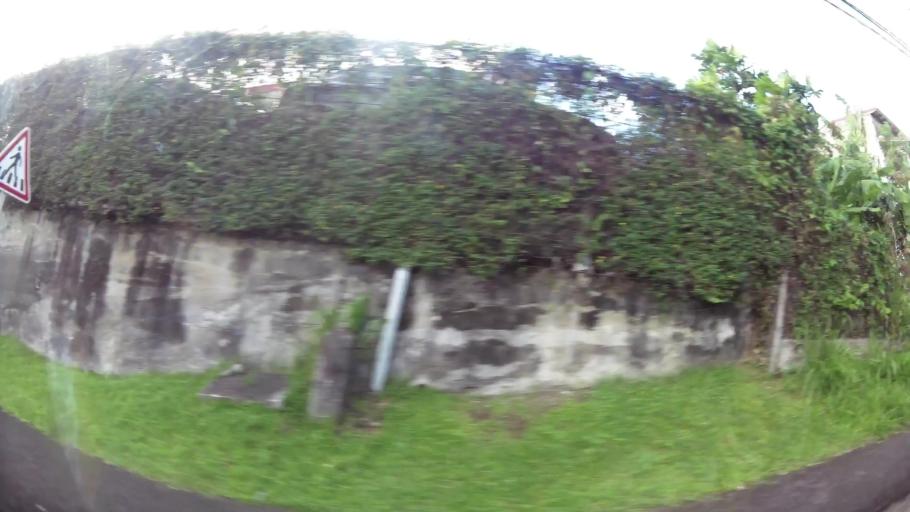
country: MQ
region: Martinique
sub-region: Martinique
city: Fort-de-France
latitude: 14.6231
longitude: -61.0608
